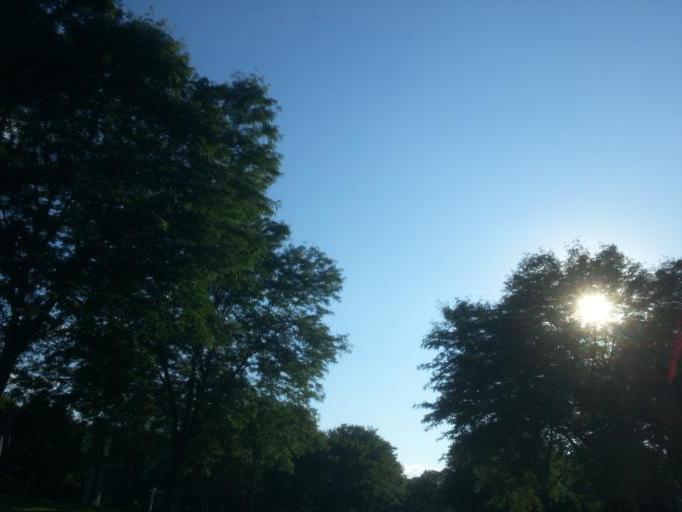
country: US
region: Wisconsin
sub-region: Dane County
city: Middleton
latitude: 43.0874
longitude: -89.4887
